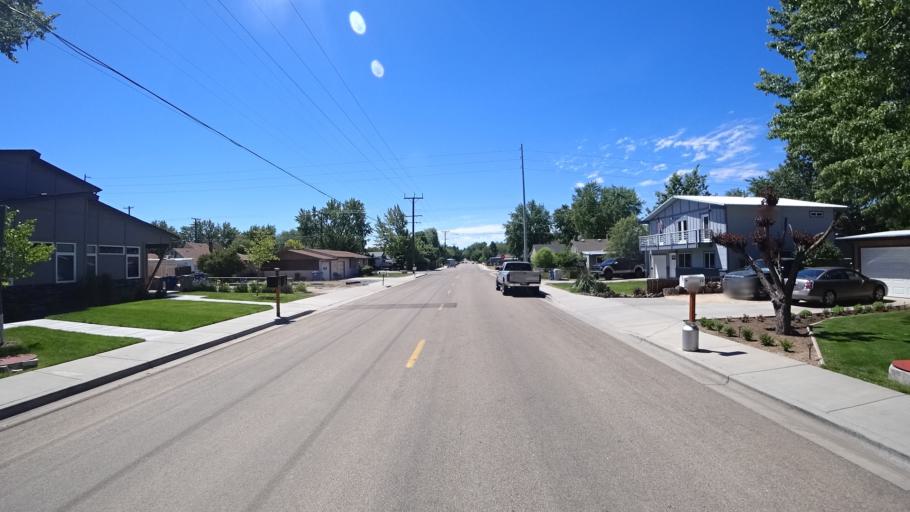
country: US
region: Idaho
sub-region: Ada County
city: Garden City
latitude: 43.5879
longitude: -116.2286
